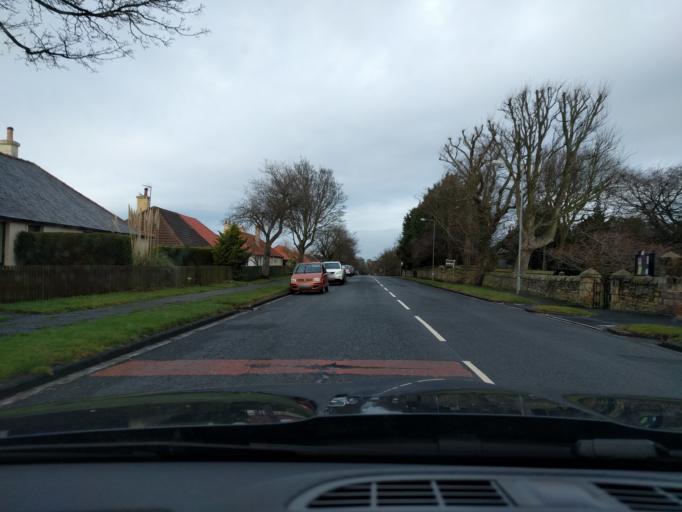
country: GB
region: England
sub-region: Northumberland
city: Ancroft
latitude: 55.7365
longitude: -1.9912
